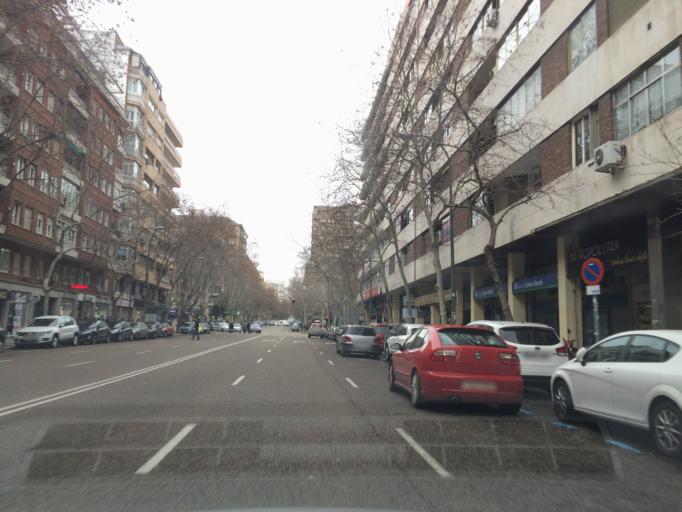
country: ES
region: Madrid
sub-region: Provincia de Madrid
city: Chamberi
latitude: 40.4512
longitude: -3.6951
